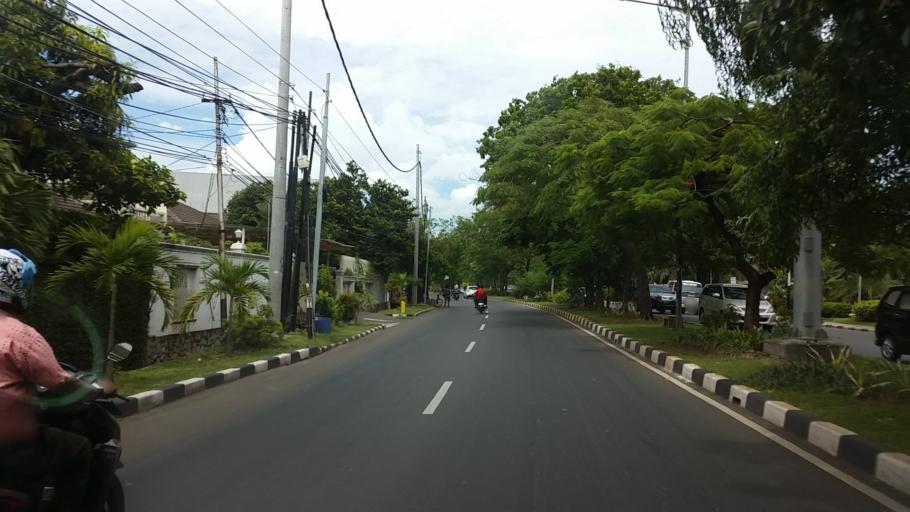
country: ID
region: Jakarta Raya
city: Jakarta
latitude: -6.1143
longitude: 106.7945
